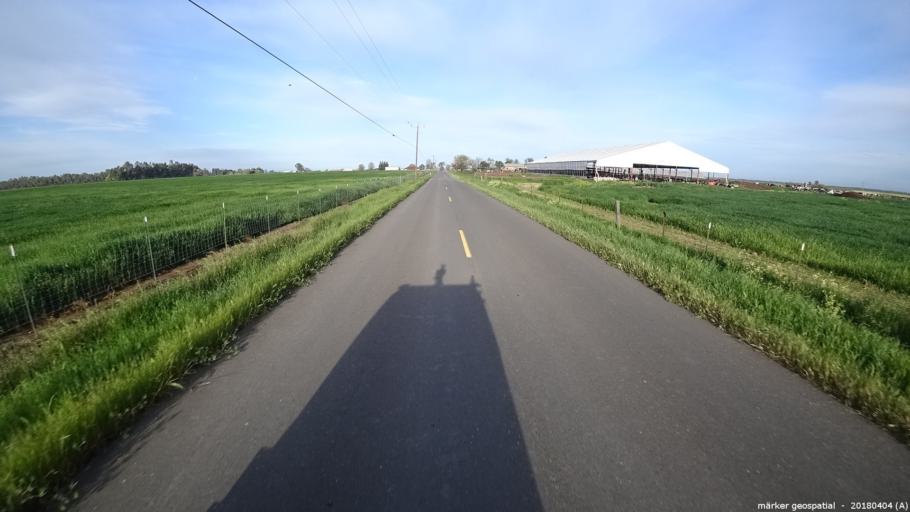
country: US
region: California
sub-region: Sacramento County
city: Herald
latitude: 38.3363
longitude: -121.2840
